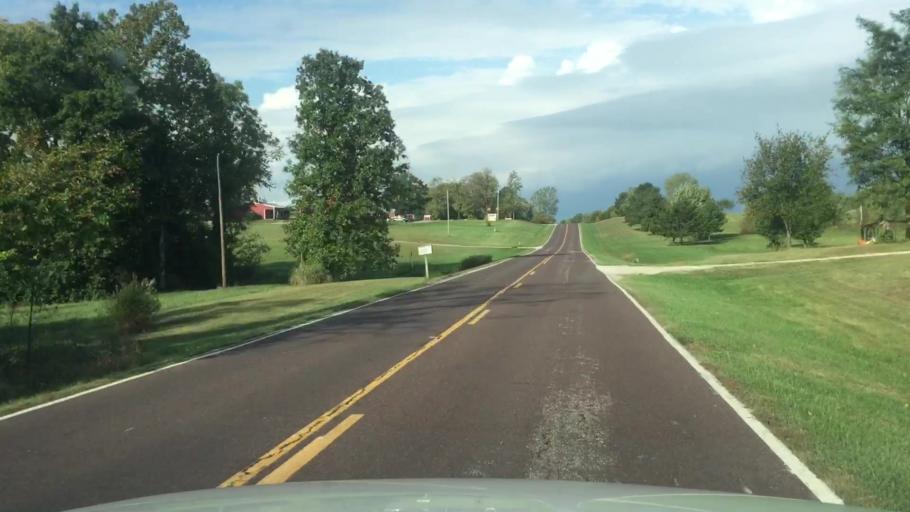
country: US
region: Missouri
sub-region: Boone County
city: Ashland
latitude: 38.8691
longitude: -92.2807
